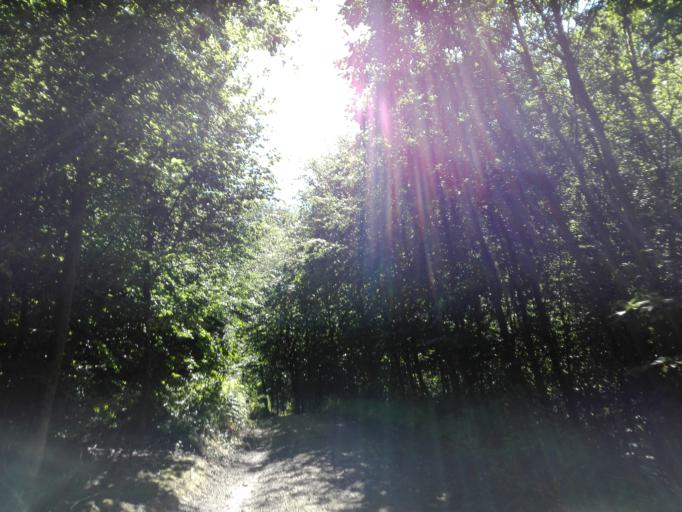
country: DK
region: Central Jutland
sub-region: Odder Kommune
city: Odder
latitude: 55.9513
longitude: 10.1384
